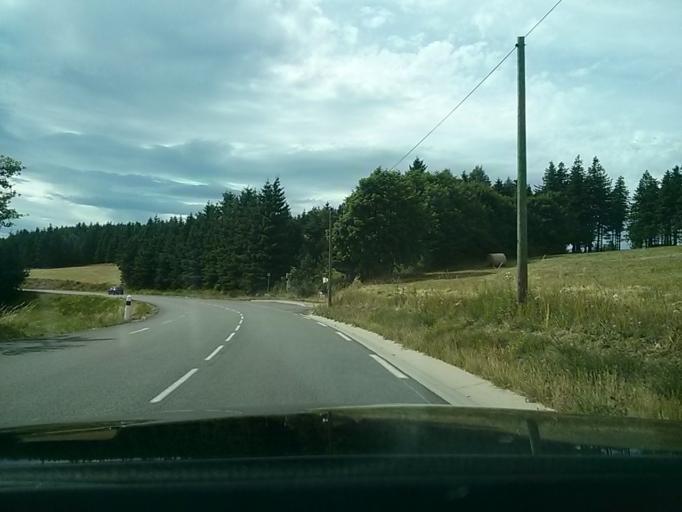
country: FR
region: Rhone-Alpes
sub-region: Departement de la Loire
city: Saint-Genest-Malifaux
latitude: 45.3727
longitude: 4.5041
